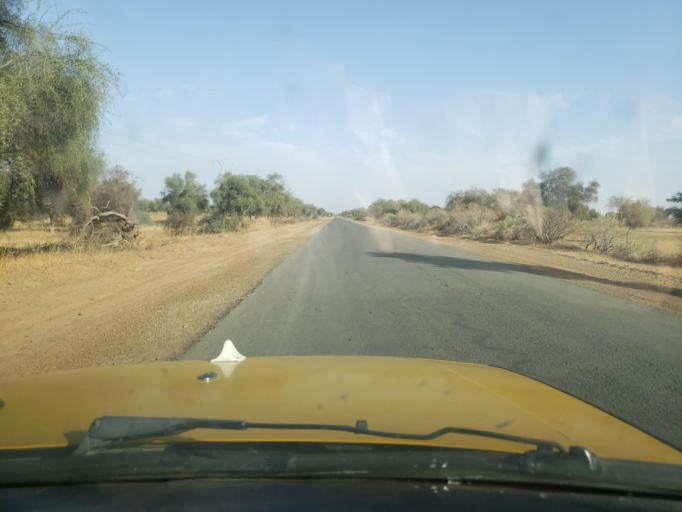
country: SN
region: Louga
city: Louga
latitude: 15.5028
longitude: -15.9470
